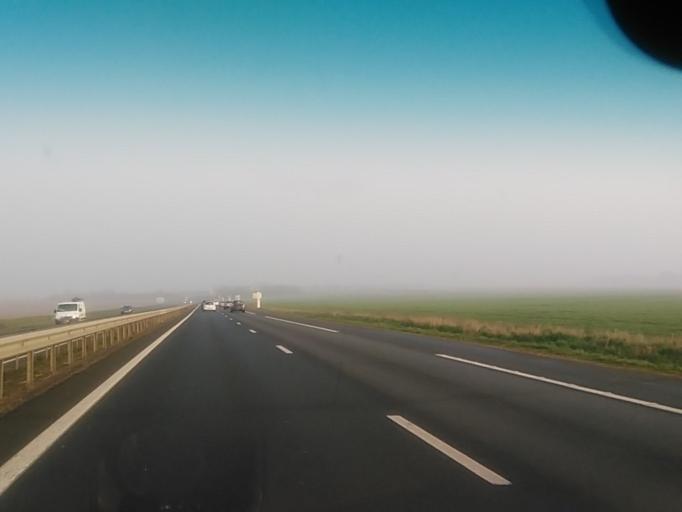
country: FR
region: Lower Normandy
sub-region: Departement du Calvados
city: Bourguebus
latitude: 49.1162
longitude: -0.3220
